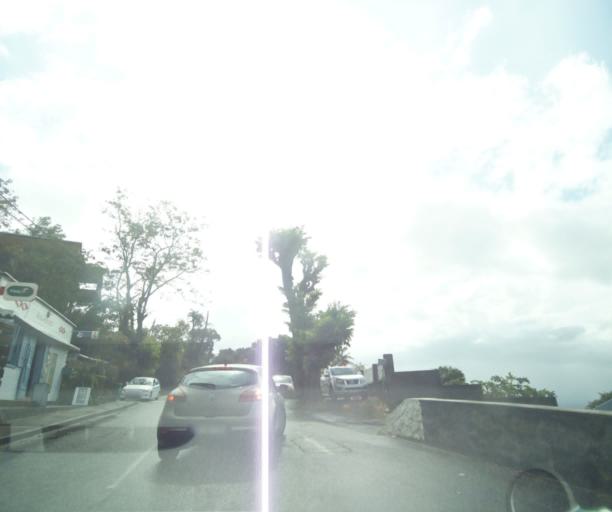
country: RE
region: Reunion
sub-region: Reunion
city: Saint-Paul
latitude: -20.9969
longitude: 55.3276
